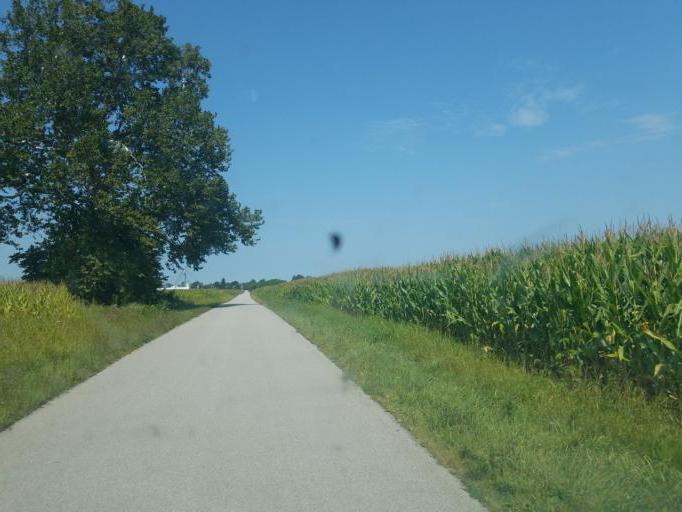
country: US
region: Ohio
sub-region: Crawford County
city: Bucyrus
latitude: 40.7808
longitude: -83.1119
